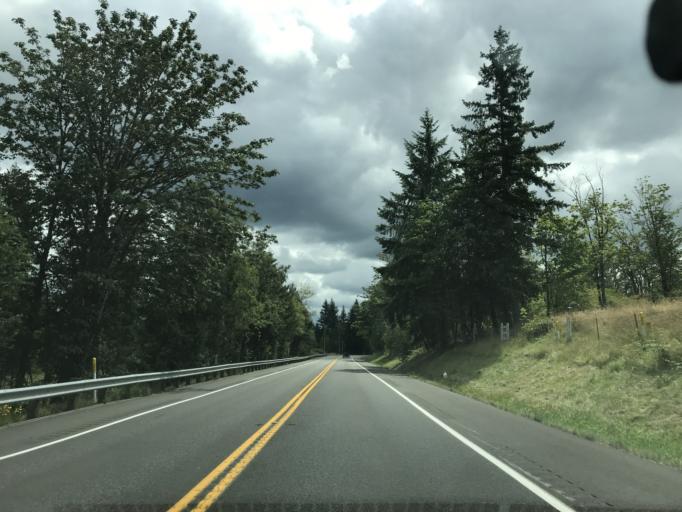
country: US
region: Washington
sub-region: King County
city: Maple Valley
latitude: 47.4061
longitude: -122.0504
